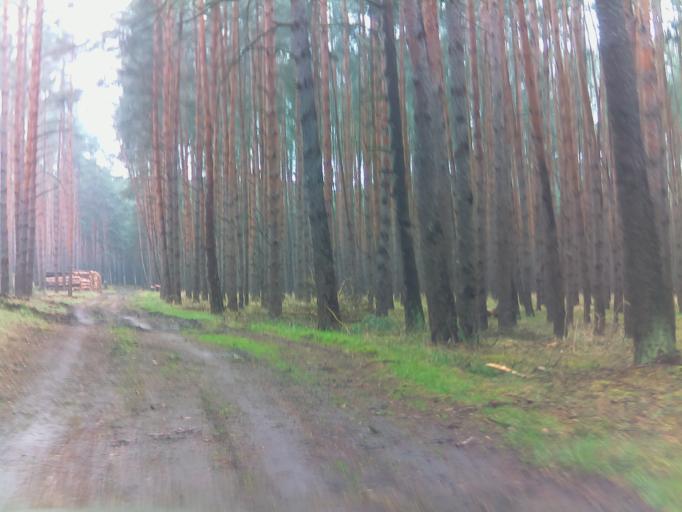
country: DE
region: Brandenburg
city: Schlepzig
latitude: 52.0162
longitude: 13.9858
